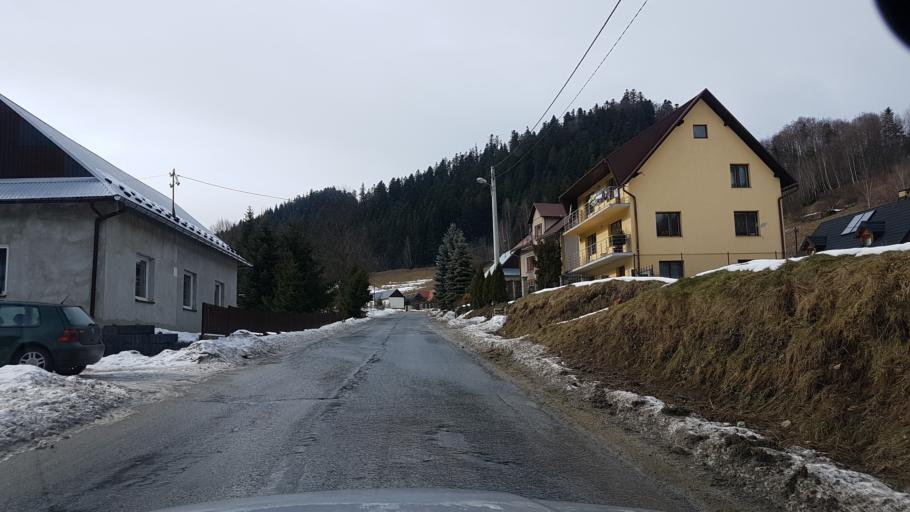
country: PL
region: Lesser Poland Voivodeship
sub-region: Powiat nowosadecki
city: Piwniczna-Zdroj
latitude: 49.4247
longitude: 20.6566
